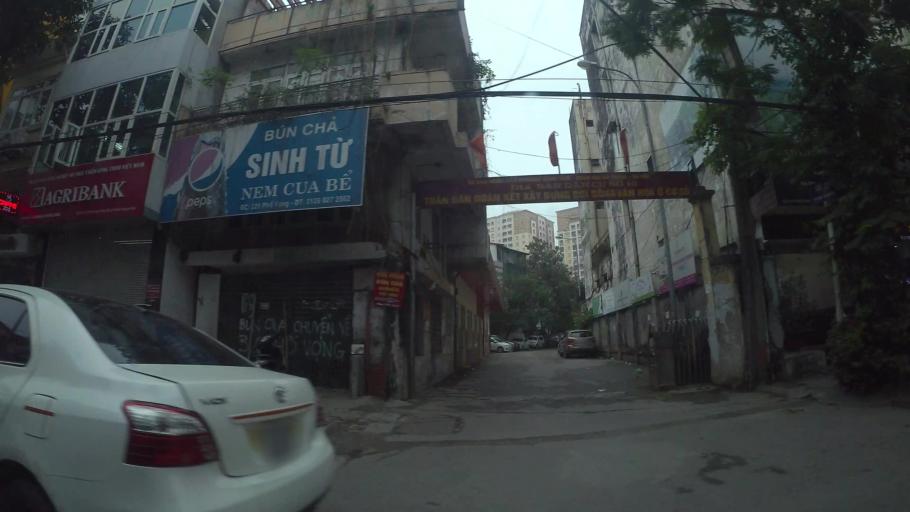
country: VN
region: Ha Noi
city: Hai BaTrung
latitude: 20.9958
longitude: 105.8429
